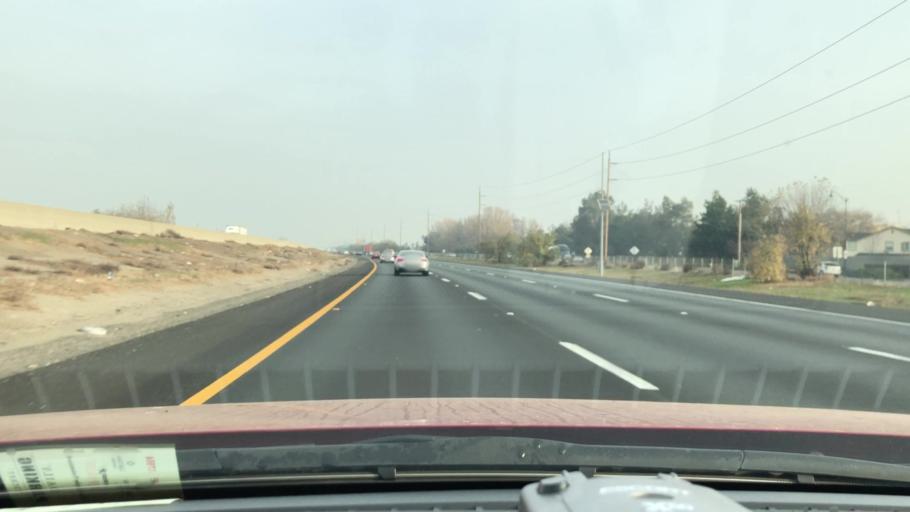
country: US
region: California
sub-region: San Joaquin County
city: Lathrop
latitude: 37.8324
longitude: -121.2876
